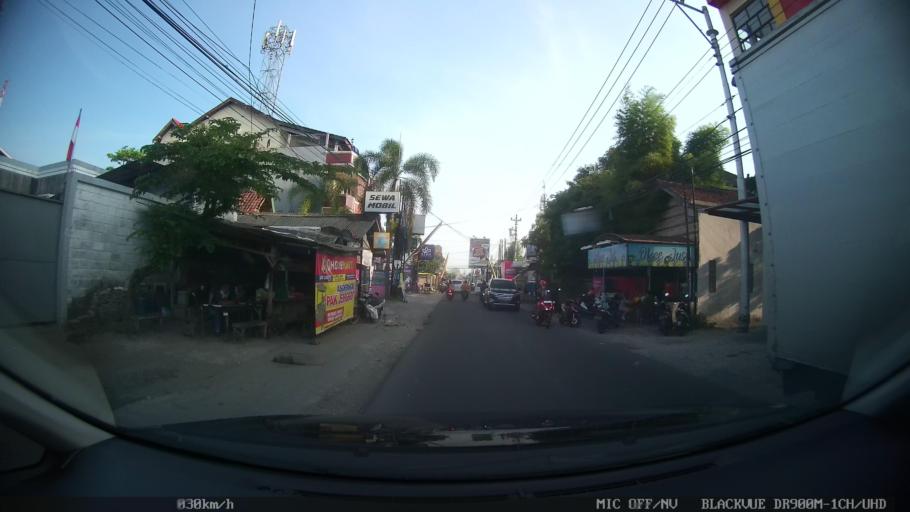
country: ID
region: Daerah Istimewa Yogyakarta
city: Depok
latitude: -7.7702
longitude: 110.4052
